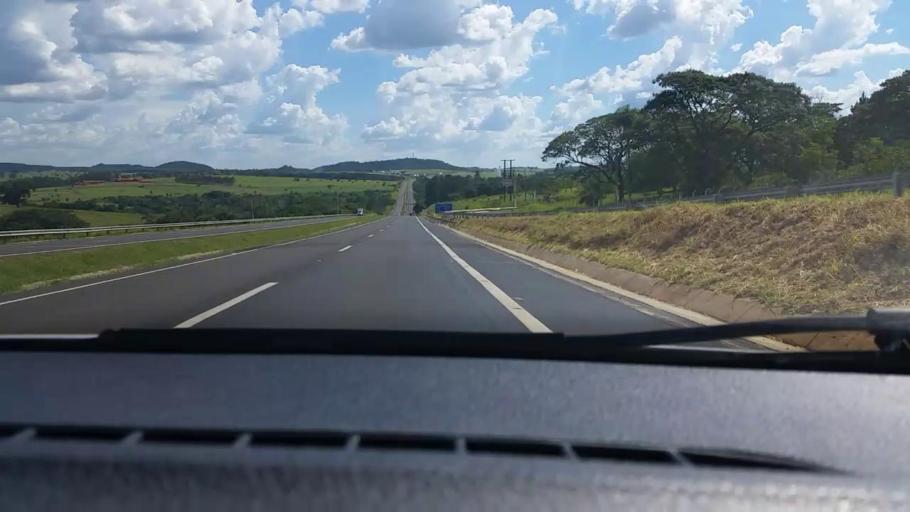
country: BR
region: Sao Paulo
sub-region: Bauru
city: Bauru
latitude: -22.4003
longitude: -49.0903
